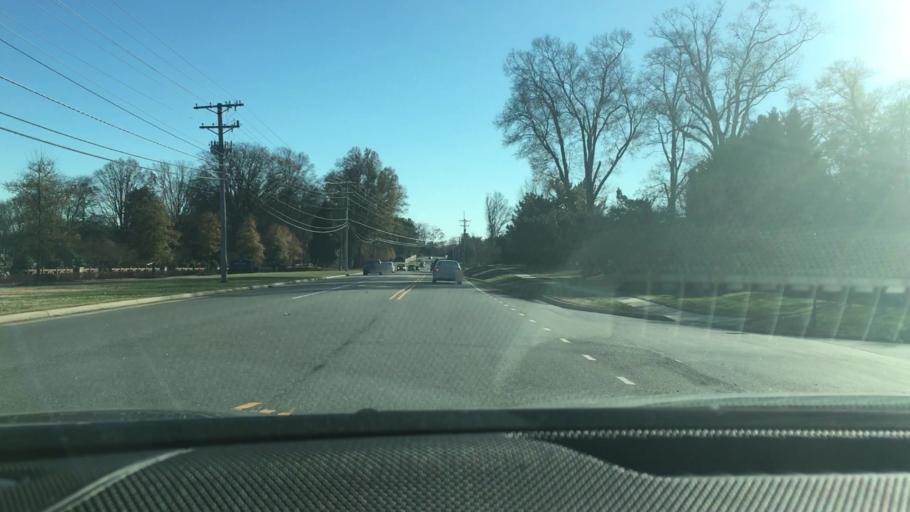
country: US
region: North Carolina
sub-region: Mecklenburg County
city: Cornelius
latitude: 35.4570
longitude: -80.8886
